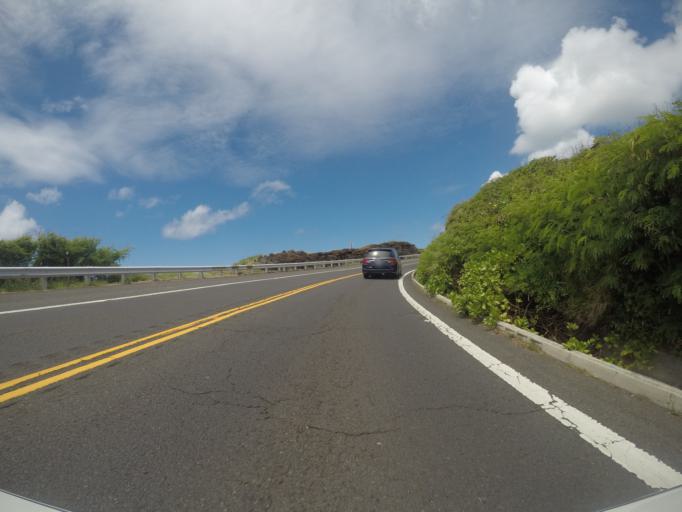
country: US
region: Hawaii
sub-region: Honolulu County
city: Waimanalo Beach
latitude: 21.2733
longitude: -157.6886
